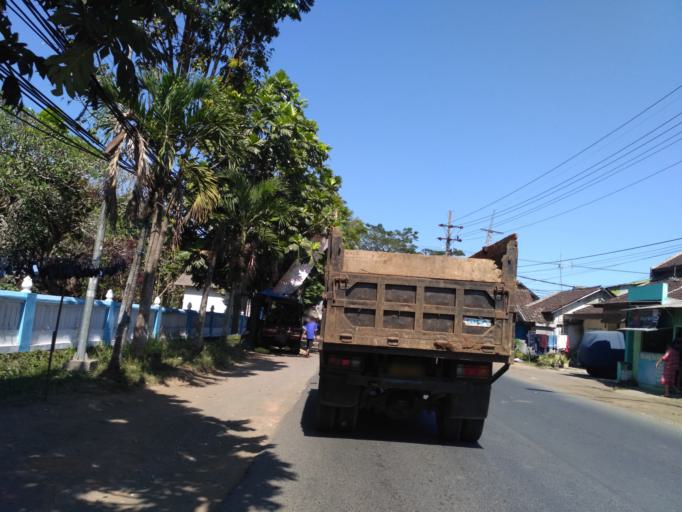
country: ID
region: East Java
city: Malang
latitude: -7.9712
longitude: 112.6737
